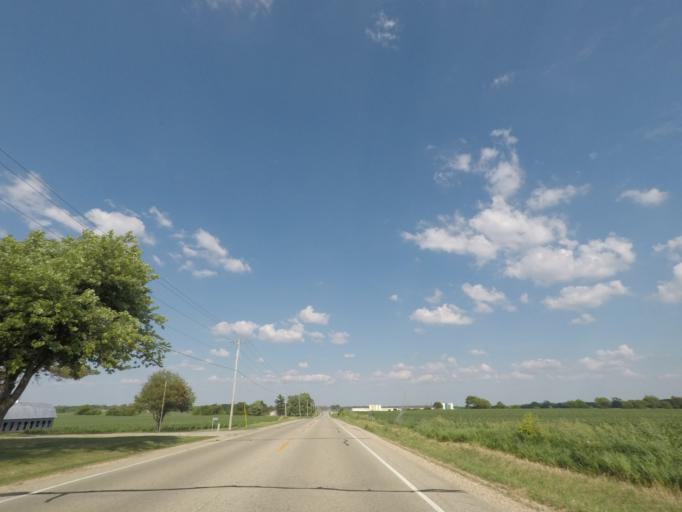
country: US
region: Wisconsin
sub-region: Walworth County
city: East Troy
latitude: 42.7927
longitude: -88.4530
